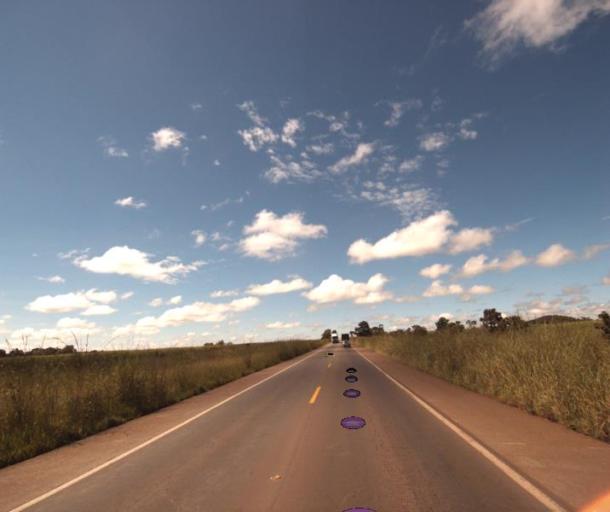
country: BR
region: Goias
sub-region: Rialma
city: Rialma
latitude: -15.4171
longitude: -49.5219
